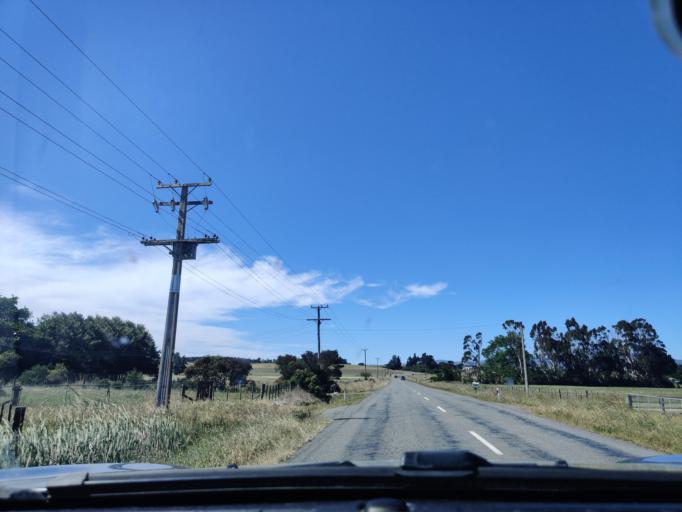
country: NZ
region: Wellington
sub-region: South Wairarapa District
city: Waipawa
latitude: -41.1948
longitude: 175.3607
